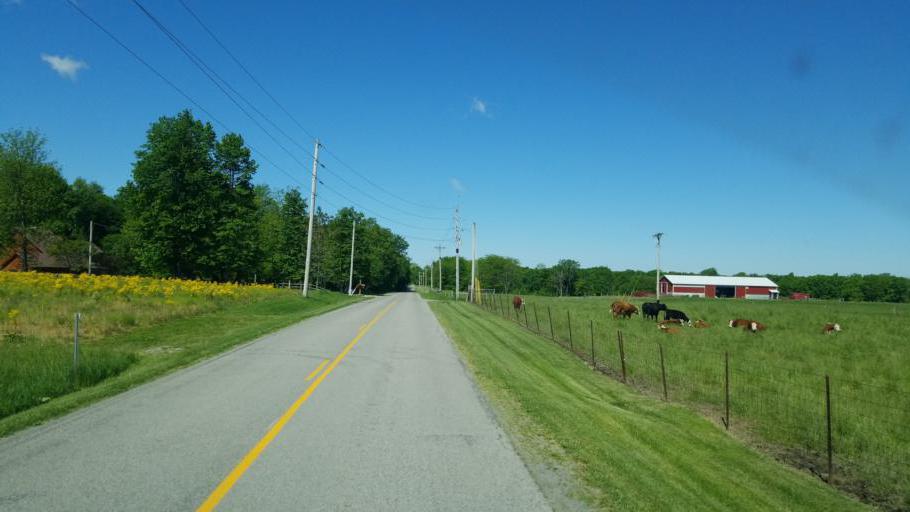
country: US
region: Ohio
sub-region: Logan County
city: Northwood
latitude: 40.4429
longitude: -83.6682
